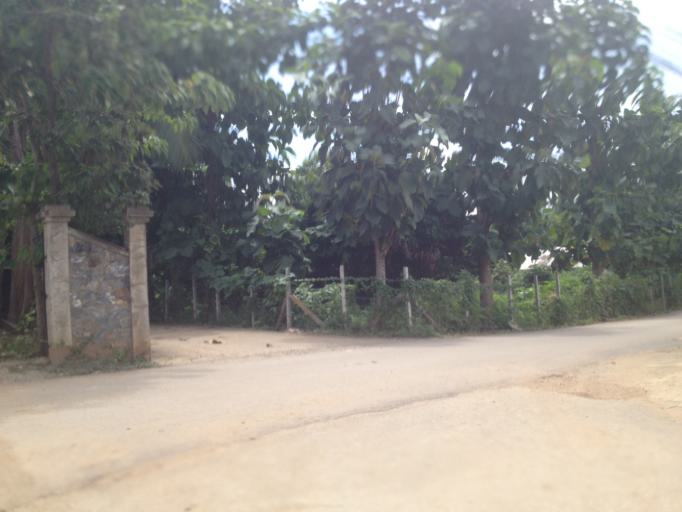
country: TH
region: Chiang Mai
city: Hang Dong
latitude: 18.7538
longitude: 98.8861
